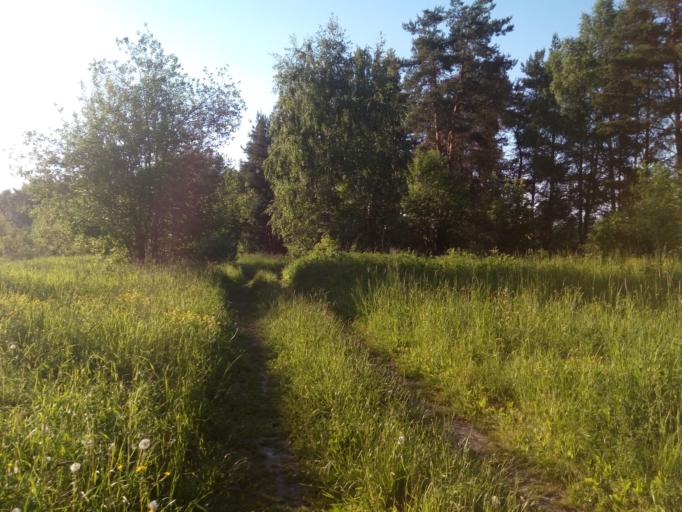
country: RU
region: Nizjnij Novgorod
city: Voskresenskoye
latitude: 56.7845
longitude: 45.5217
